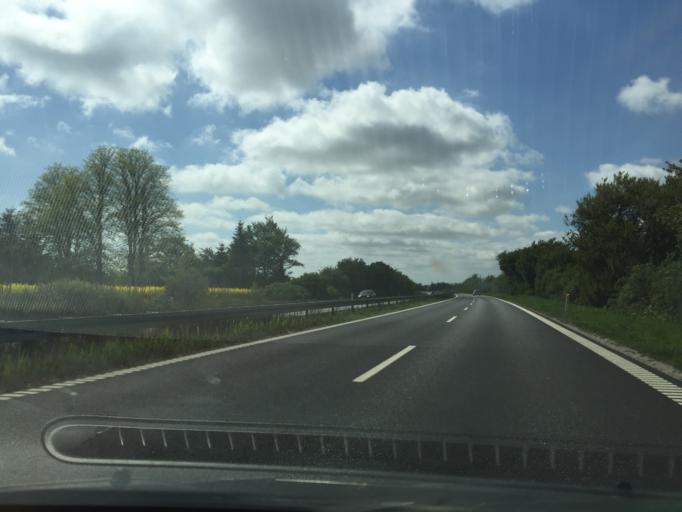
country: DK
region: Zealand
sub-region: Guldborgsund Kommune
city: Sakskobing
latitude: 54.7928
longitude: 11.6248
